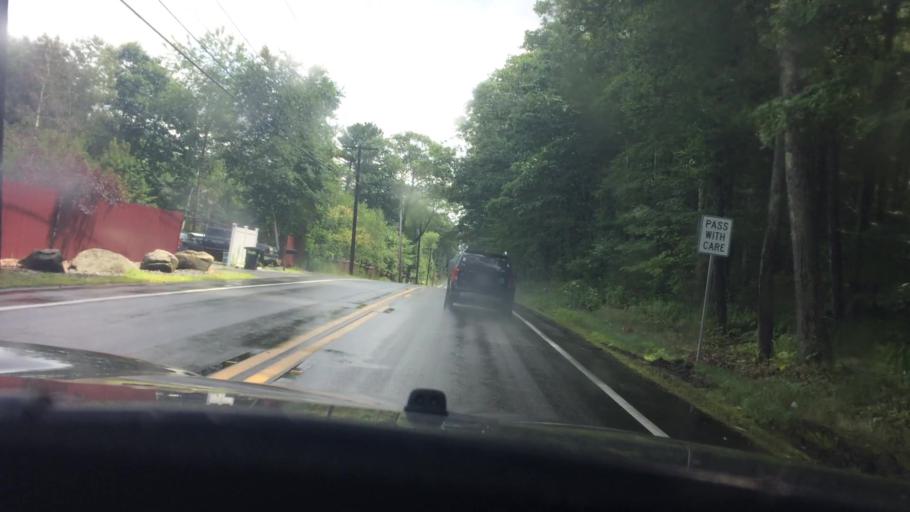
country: US
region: Massachusetts
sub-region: Worcester County
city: Phillipston
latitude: 42.5708
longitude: -72.1455
